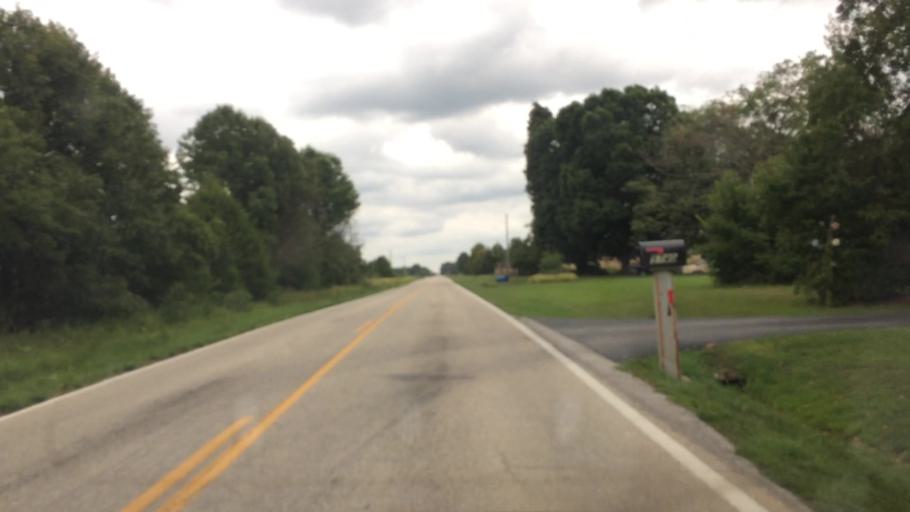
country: US
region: Missouri
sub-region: Greene County
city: Strafford
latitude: 37.3006
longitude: -93.1690
